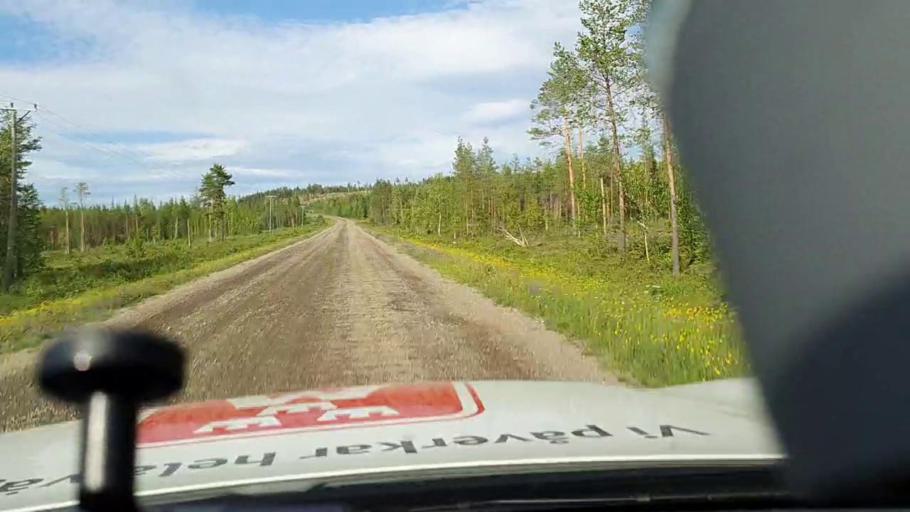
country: SE
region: Norrbotten
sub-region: Alvsbyns Kommun
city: AElvsbyn
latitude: 66.1619
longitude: 21.0500
